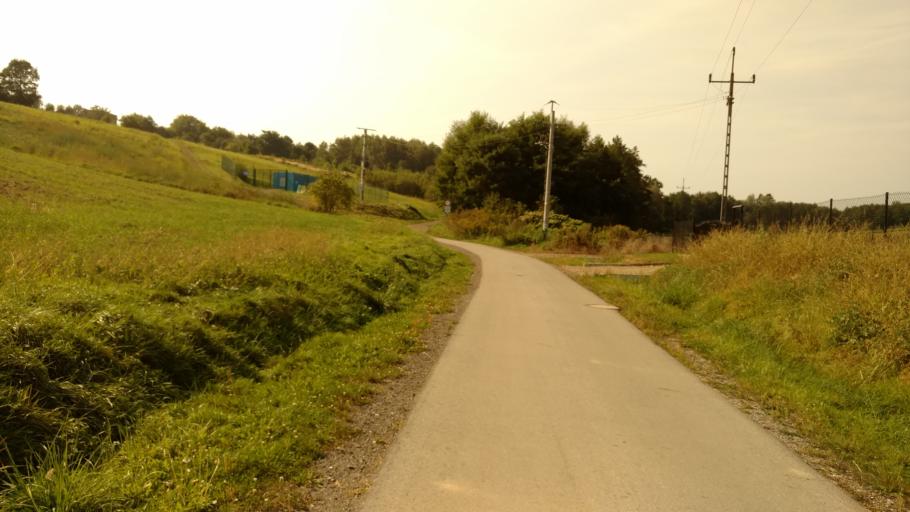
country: PL
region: Lesser Poland Voivodeship
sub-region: Powiat krakowski
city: Michalowice
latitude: 50.1291
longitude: 19.9814
